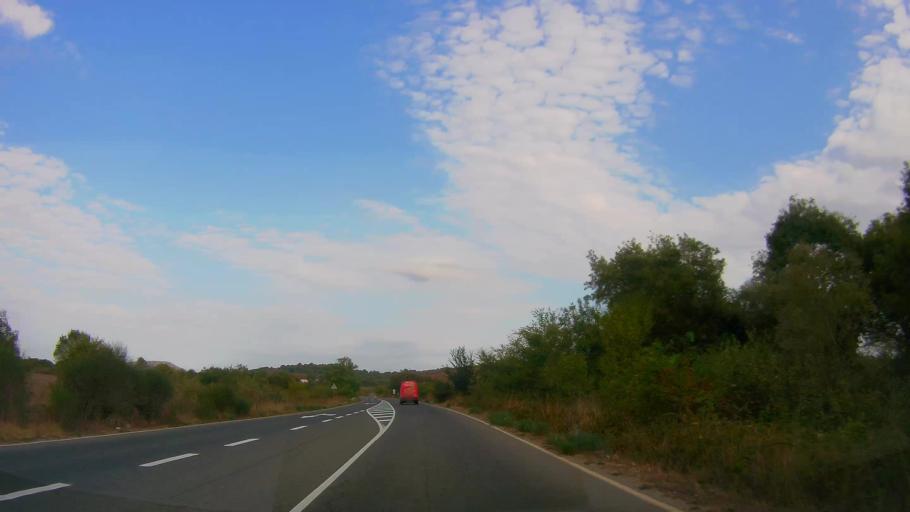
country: BG
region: Burgas
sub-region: Obshtina Sozopol
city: Sozopol
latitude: 42.3620
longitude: 27.6998
